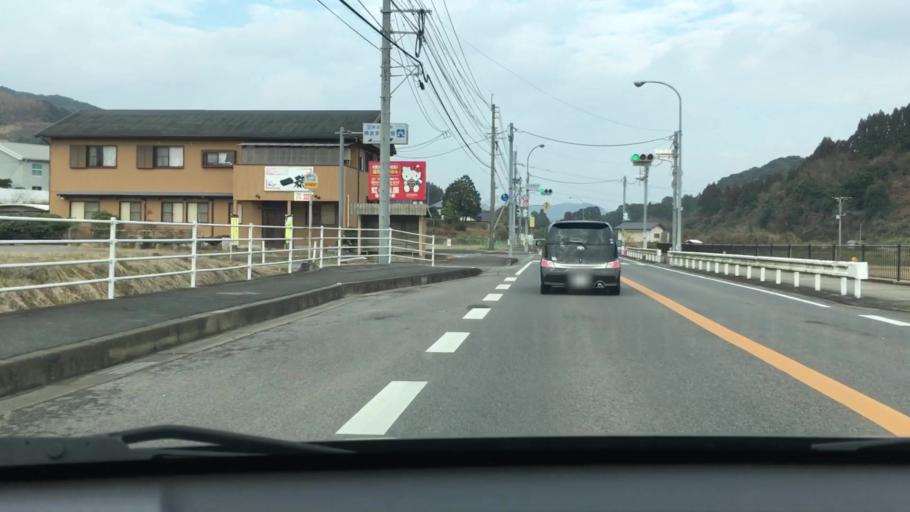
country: JP
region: Saga Prefecture
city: Imaricho-ko
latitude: 33.3166
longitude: 129.9289
